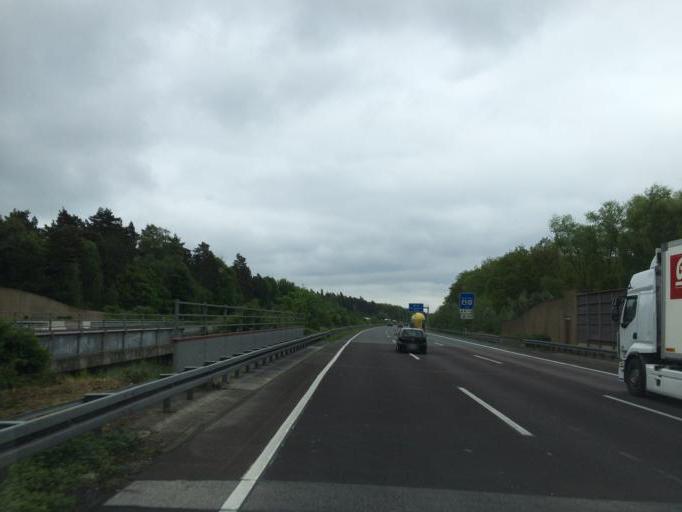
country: DE
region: Lower Saxony
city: Mariental
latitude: 52.2686
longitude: 10.9652
